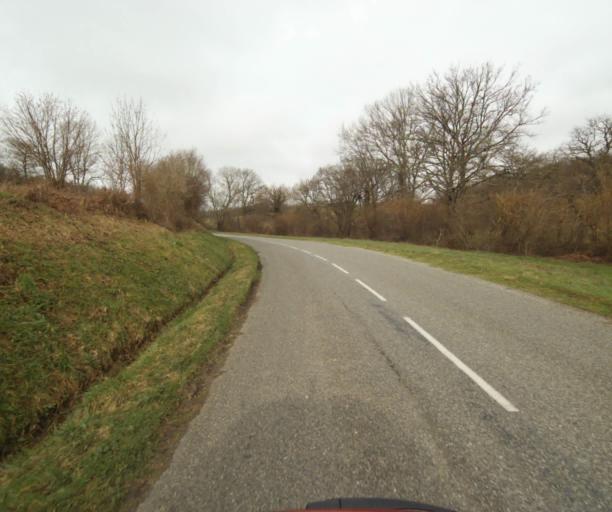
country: FR
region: Midi-Pyrenees
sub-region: Departement de l'Ariege
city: Pamiers
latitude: 43.1455
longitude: 1.5283
